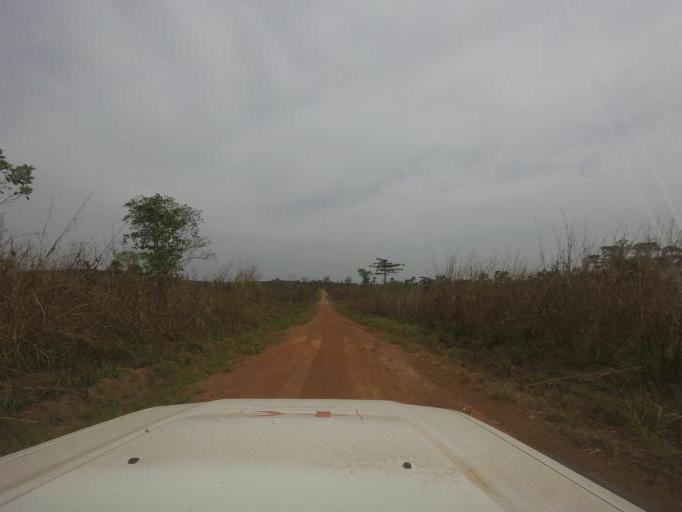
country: GN
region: Nzerekore
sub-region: Prefecture de Guekedou
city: Gueckedou
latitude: 8.4393
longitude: -10.2439
